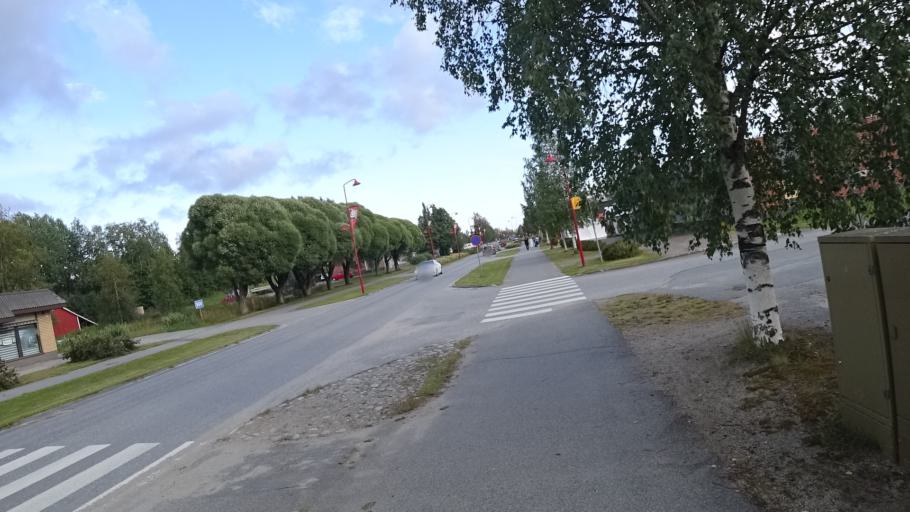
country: FI
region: North Karelia
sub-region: Joensuu
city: Ilomantsi
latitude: 62.6732
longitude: 30.9297
